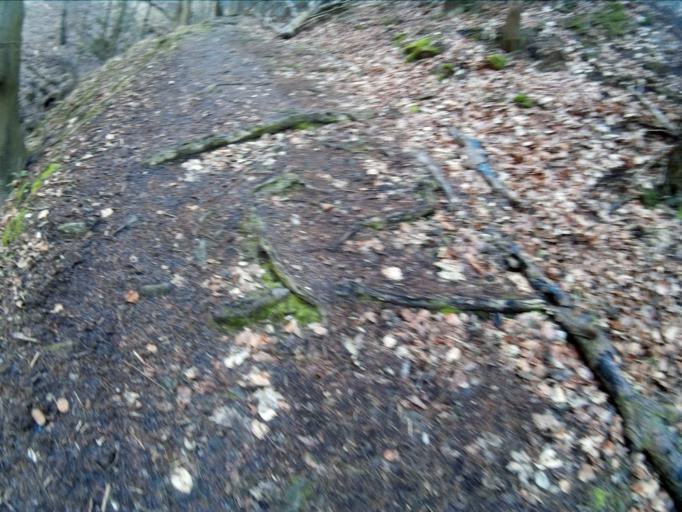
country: CZ
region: Vysocina
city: Namest' nad Oslavou
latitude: 49.1682
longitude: 16.1728
